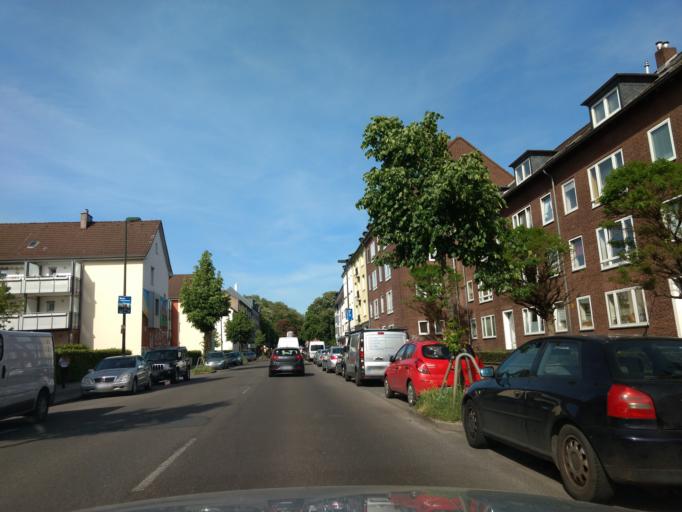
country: DE
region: North Rhine-Westphalia
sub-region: Regierungsbezirk Dusseldorf
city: Erkrath
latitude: 51.2303
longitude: 6.8482
